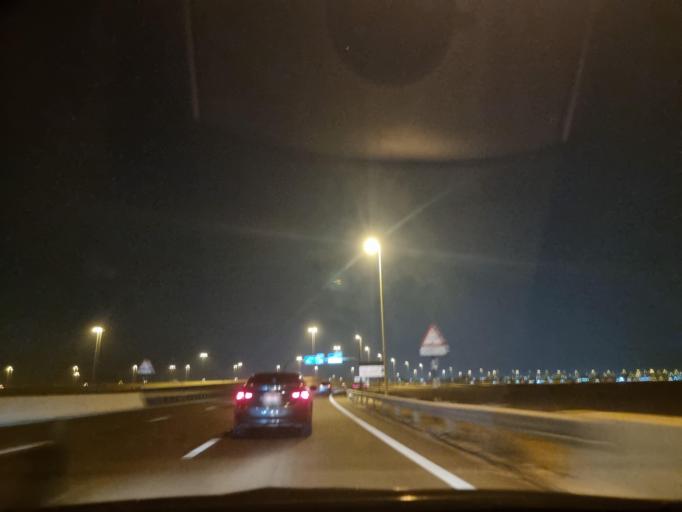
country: AE
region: Abu Dhabi
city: Abu Dhabi
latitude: 24.4130
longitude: 54.7105
